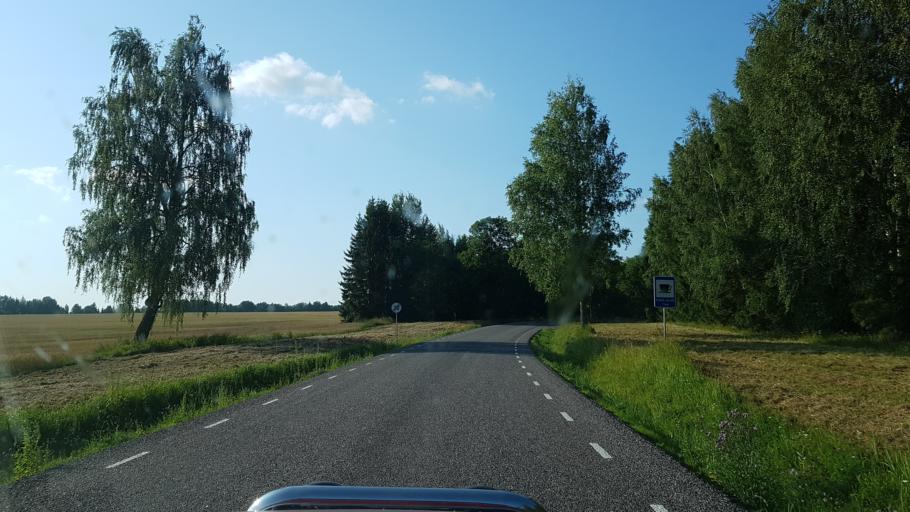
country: EE
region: Polvamaa
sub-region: Polva linn
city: Polva
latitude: 58.0026
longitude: 26.9273
